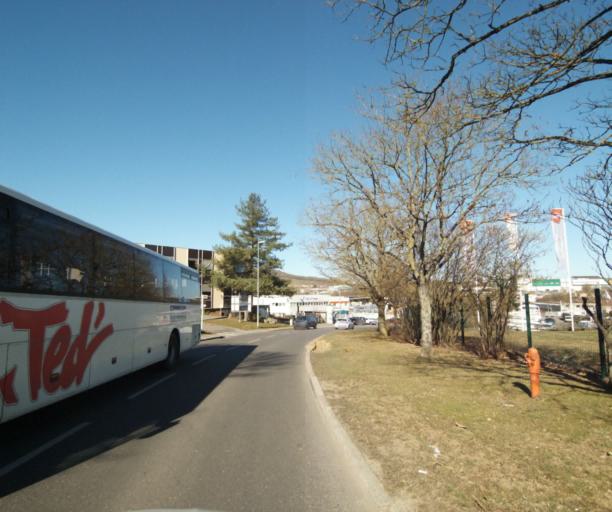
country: FR
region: Lorraine
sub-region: Departement de Meurthe-et-Moselle
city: Richardmenil
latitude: 48.6138
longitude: 6.1812
